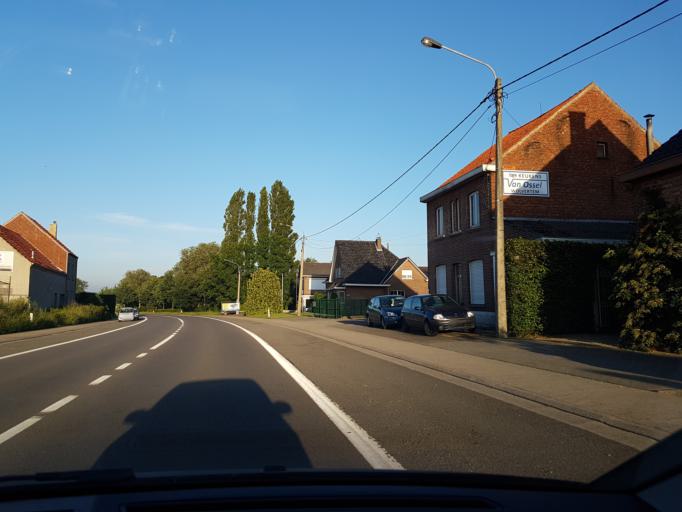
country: BE
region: Flanders
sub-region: Provincie Vlaams-Brabant
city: Merchtem
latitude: 50.9514
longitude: 4.2687
